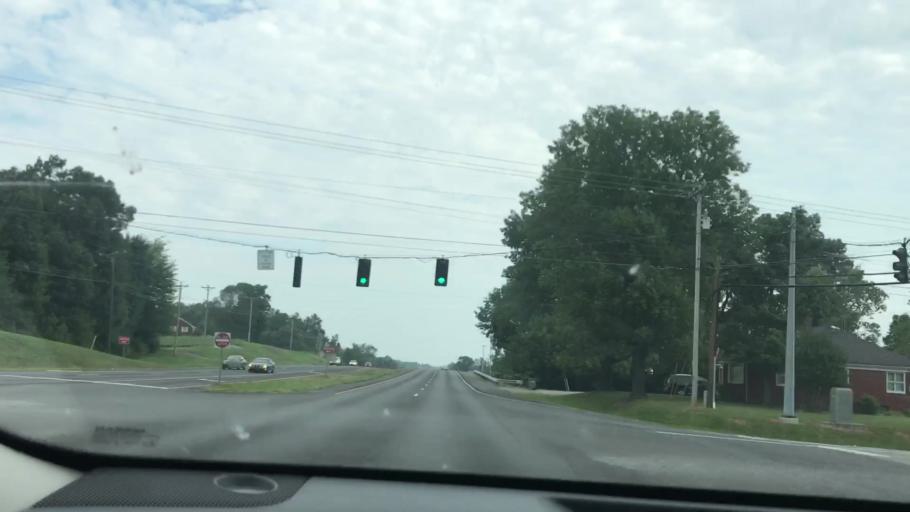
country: US
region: Kentucky
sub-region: Calloway County
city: Murray
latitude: 36.6462
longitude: -88.3079
